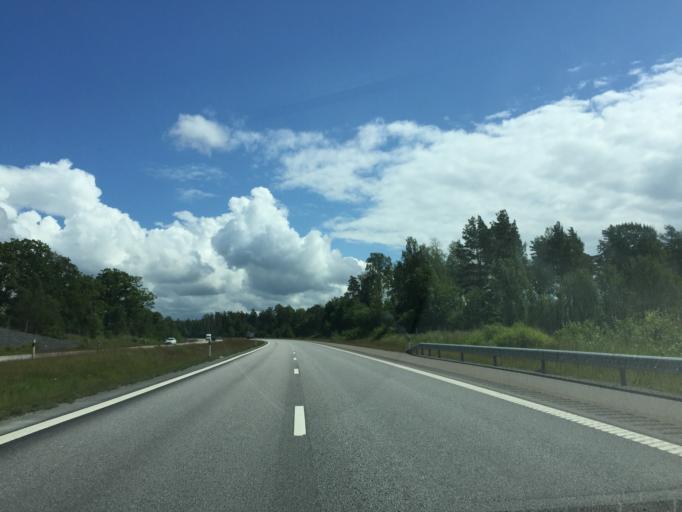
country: SE
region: OErebro
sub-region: Orebro Kommun
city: Odensbacken
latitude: 59.3168
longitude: 15.4586
